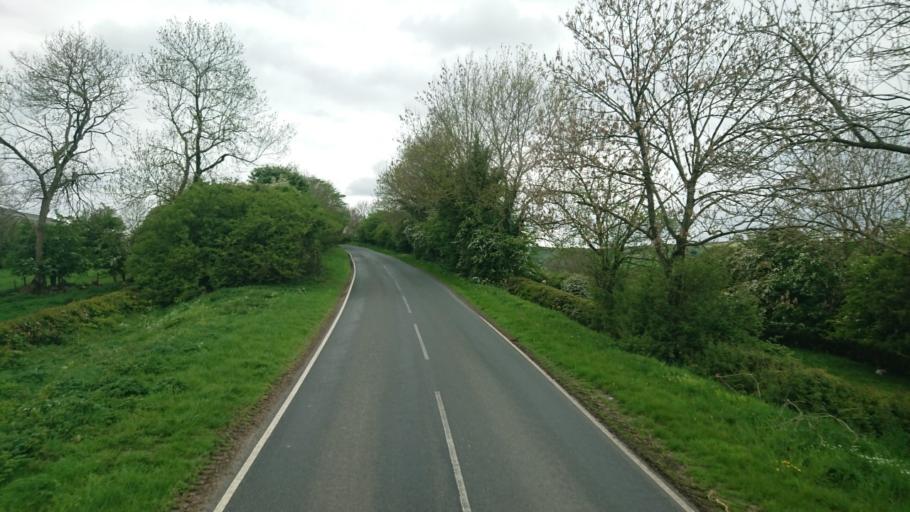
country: GB
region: England
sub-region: North Yorkshire
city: Leyburn
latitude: 54.2748
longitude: -1.9901
